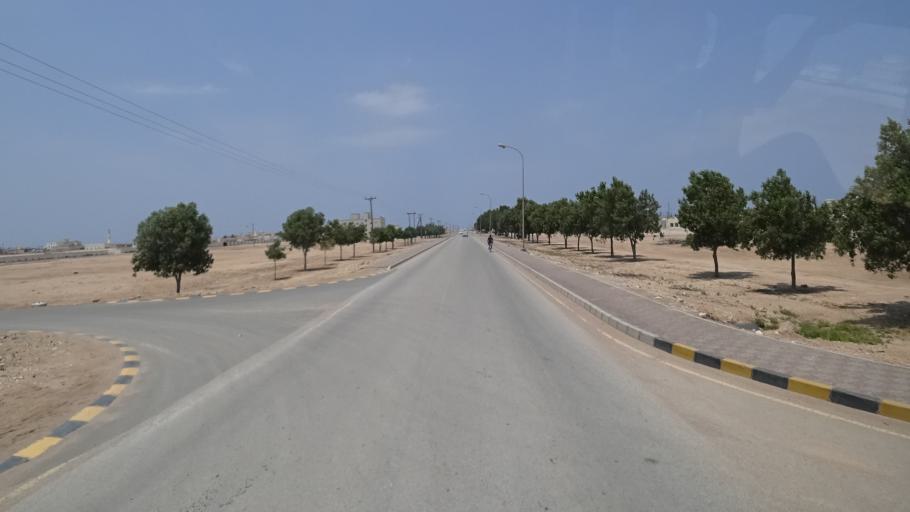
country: OM
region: Ash Sharqiyah
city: Sur
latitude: 22.5175
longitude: 59.7930
